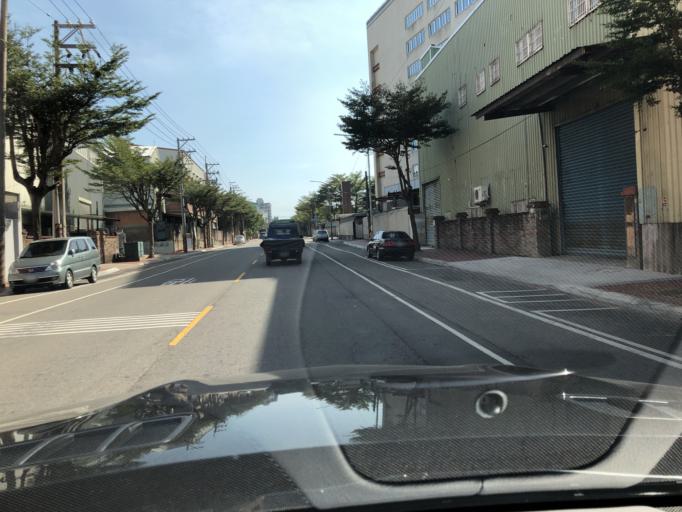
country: TW
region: Taiwan
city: Taoyuan City
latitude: 25.0727
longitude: 121.2877
